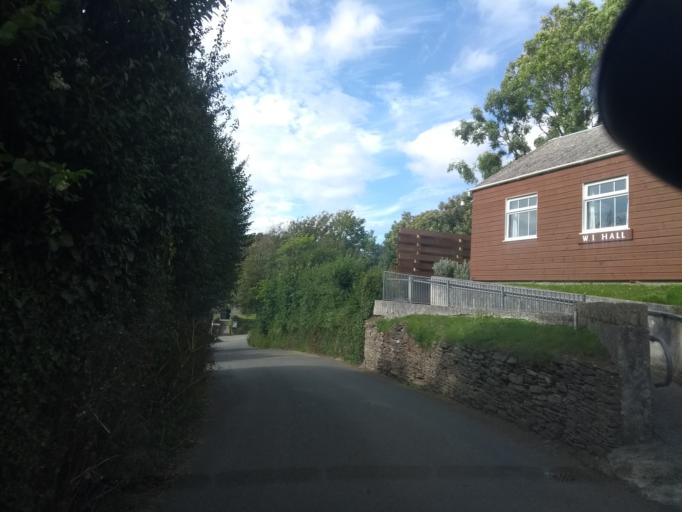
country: GB
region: England
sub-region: Devon
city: Modbury
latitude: 50.2976
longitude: -3.8930
